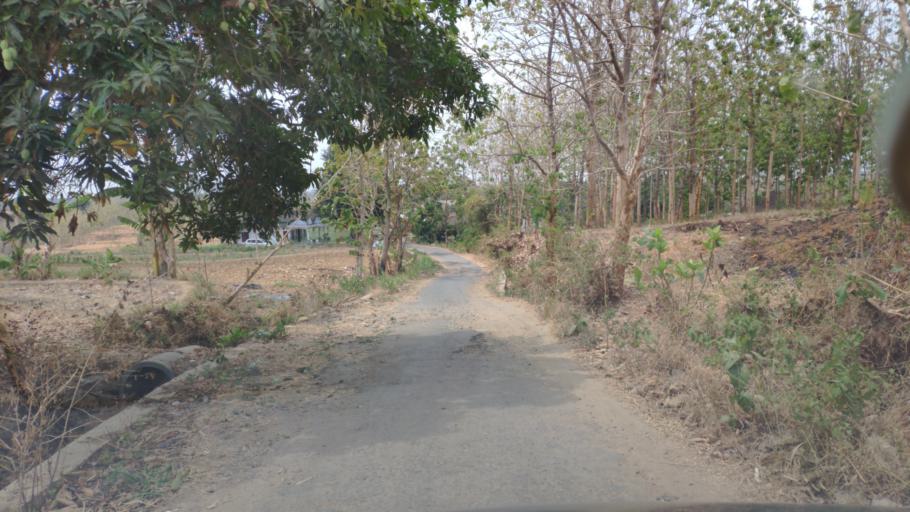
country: ID
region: Central Java
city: Kedungbacin
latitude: -6.8718
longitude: 111.2240
